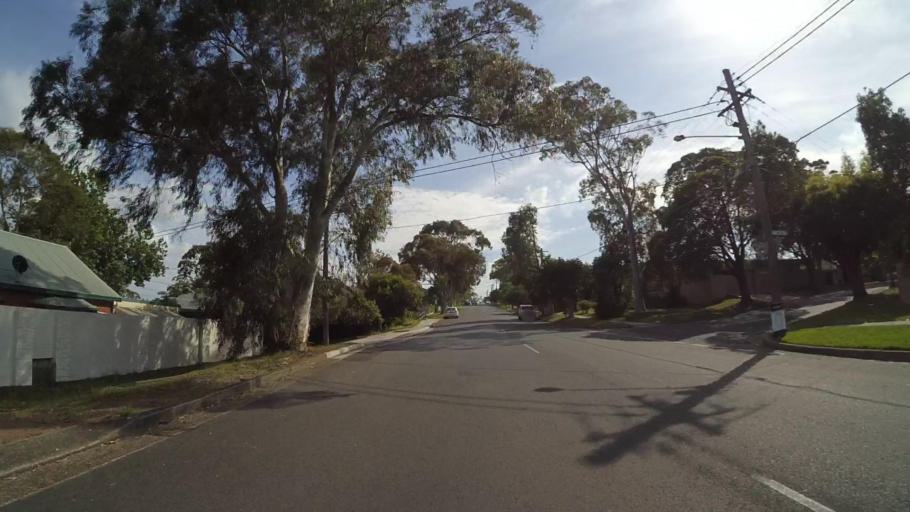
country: AU
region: New South Wales
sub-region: Sutherland Shire
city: Caringbah South
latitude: -34.0528
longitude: 151.1145
